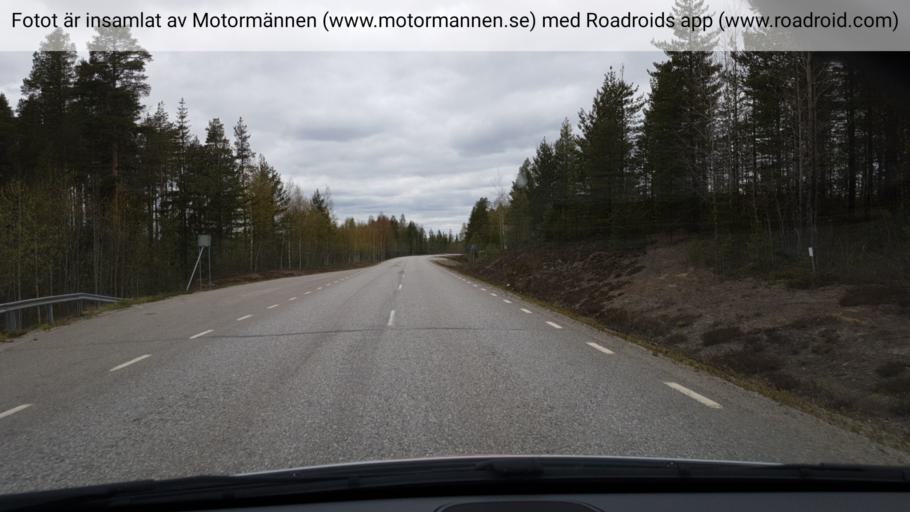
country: SE
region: Vaesterbotten
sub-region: Sorsele Kommun
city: Sorsele
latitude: 65.3102
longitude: 17.6839
